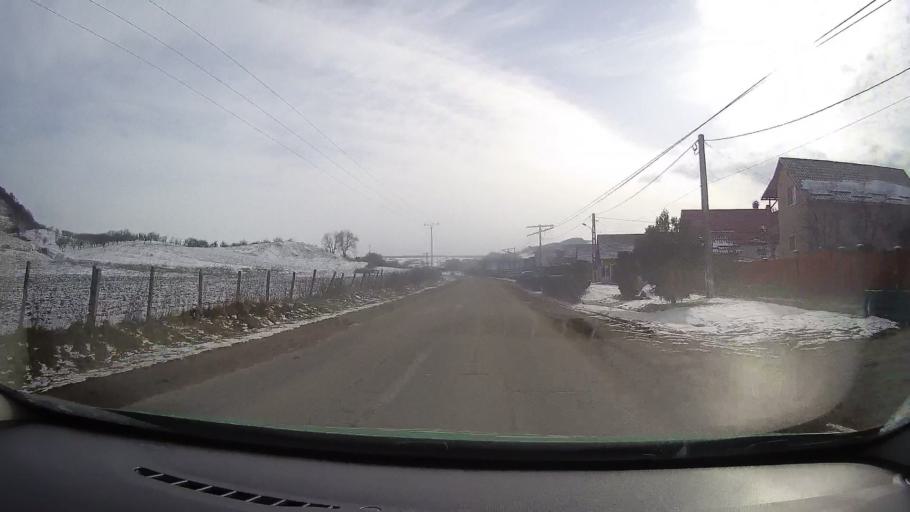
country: RO
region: Mures
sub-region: Comuna Apold
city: Apold
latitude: 46.1341
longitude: 24.8195
